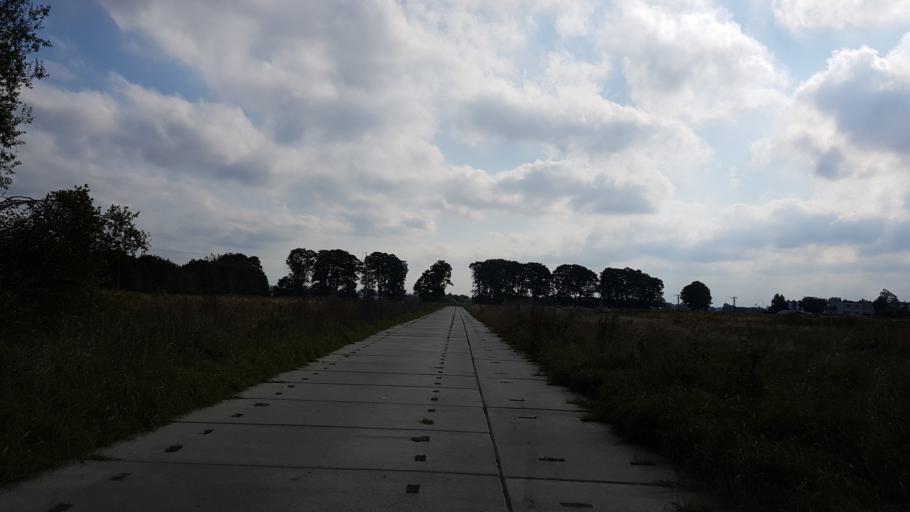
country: PL
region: West Pomeranian Voivodeship
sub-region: Koszalin
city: Koszalin
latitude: 54.1763
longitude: 16.1575
